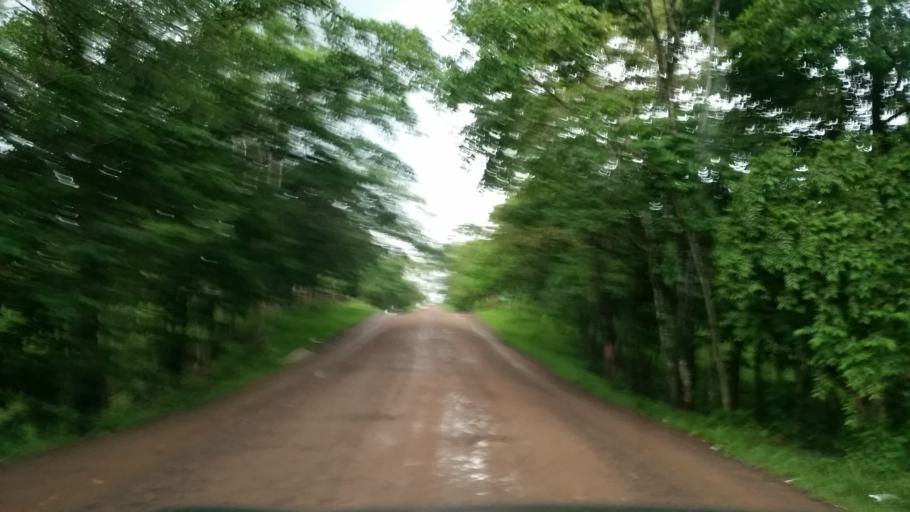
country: NI
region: Atlantico Norte (RAAN)
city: Siuna
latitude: 13.3906
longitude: -84.8564
